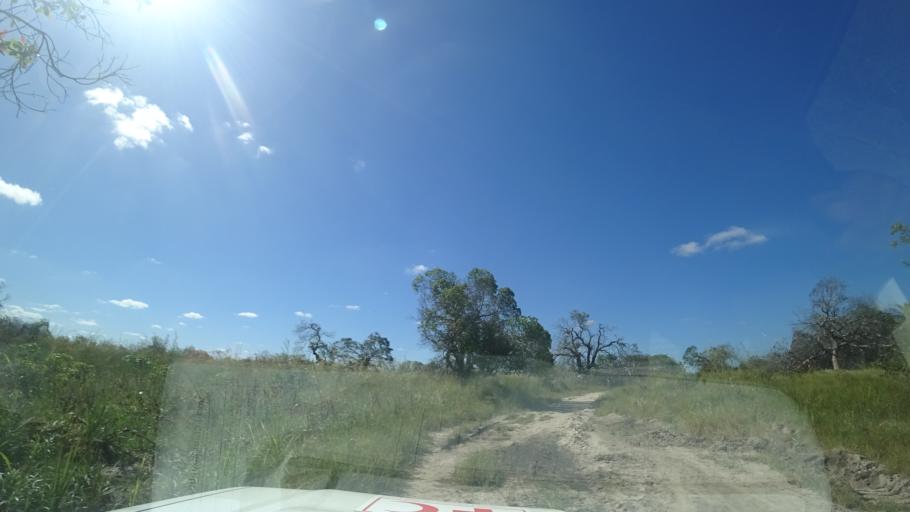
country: MZ
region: Sofala
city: Dondo
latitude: -19.4827
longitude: 34.6205
